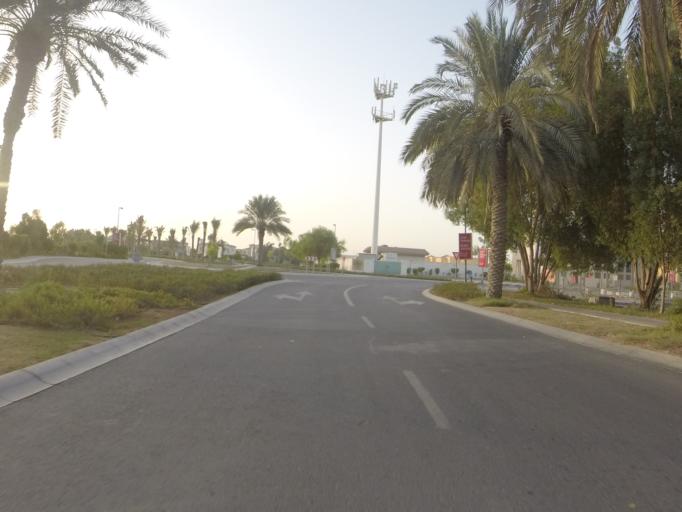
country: AE
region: Dubai
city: Dubai
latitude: 25.0615
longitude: 55.1438
